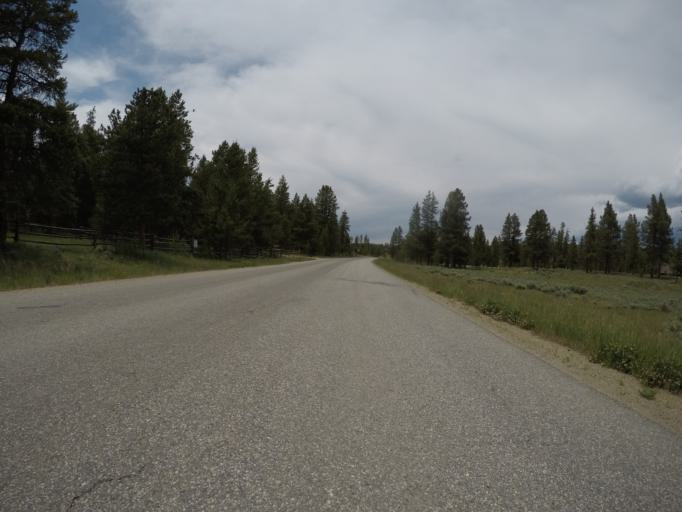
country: US
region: Colorado
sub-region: Grand County
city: Fraser
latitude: 39.9874
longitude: -105.8815
